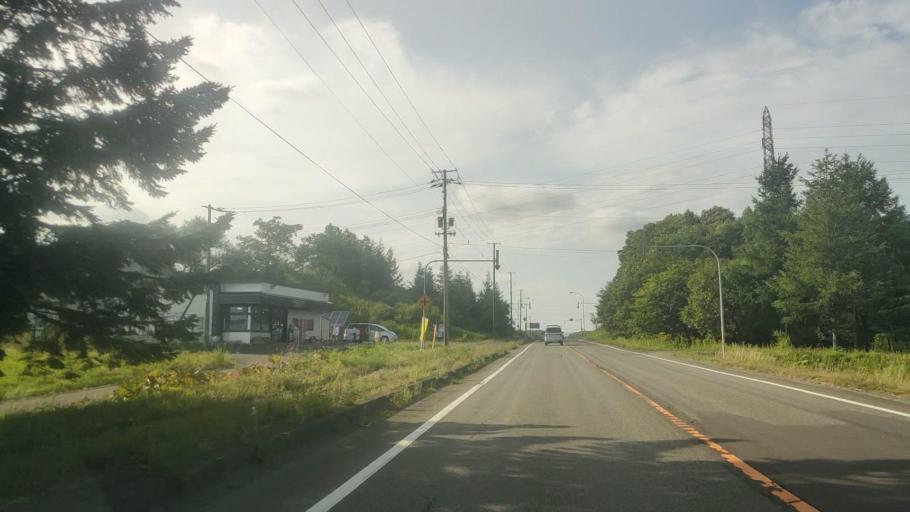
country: JP
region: Hokkaido
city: Chitose
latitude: 42.8816
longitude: 141.8143
